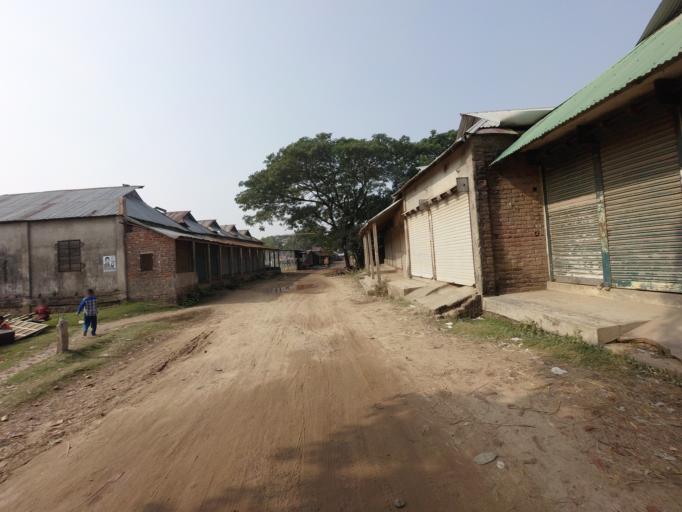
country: BD
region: Dhaka
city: Netrakona
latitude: 25.0088
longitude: 90.6821
